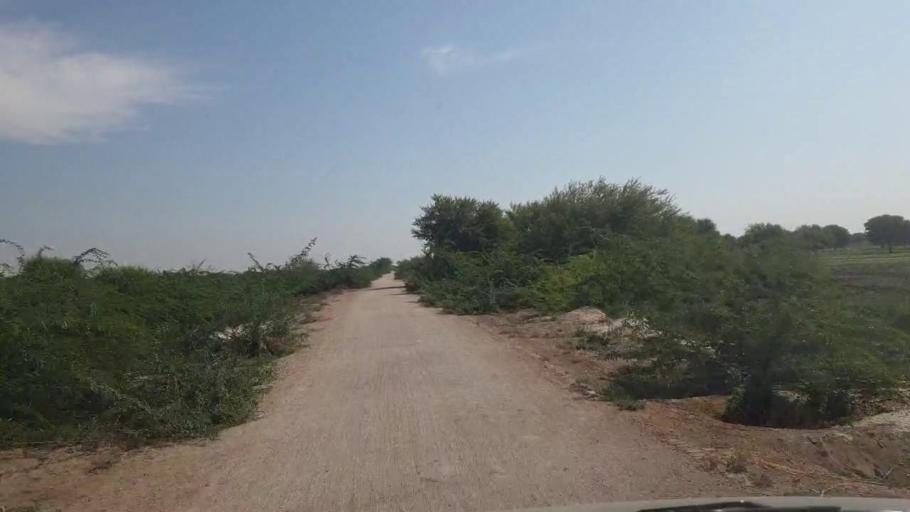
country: PK
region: Sindh
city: Digri
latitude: 24.9571
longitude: 69.1356
